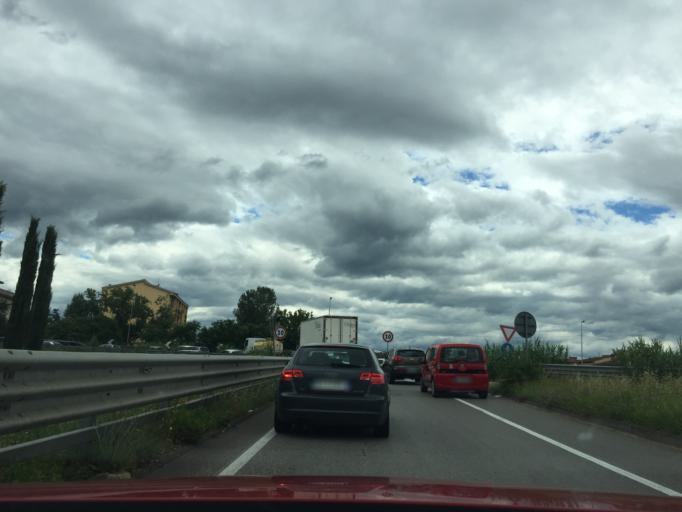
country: IT
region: Tuscany
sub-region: Province of Florence
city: Scandicci
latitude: 43.7691
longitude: 11.1882
